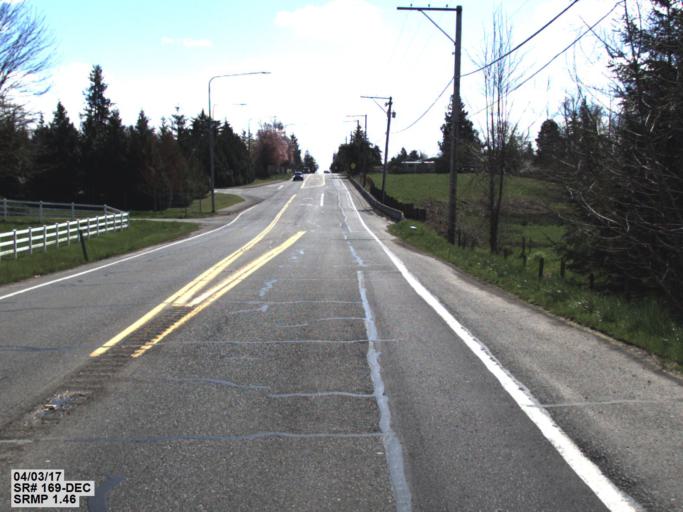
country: US
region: Washington
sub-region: King County
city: Enumclaw
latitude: 47.2254
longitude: -121.9897
